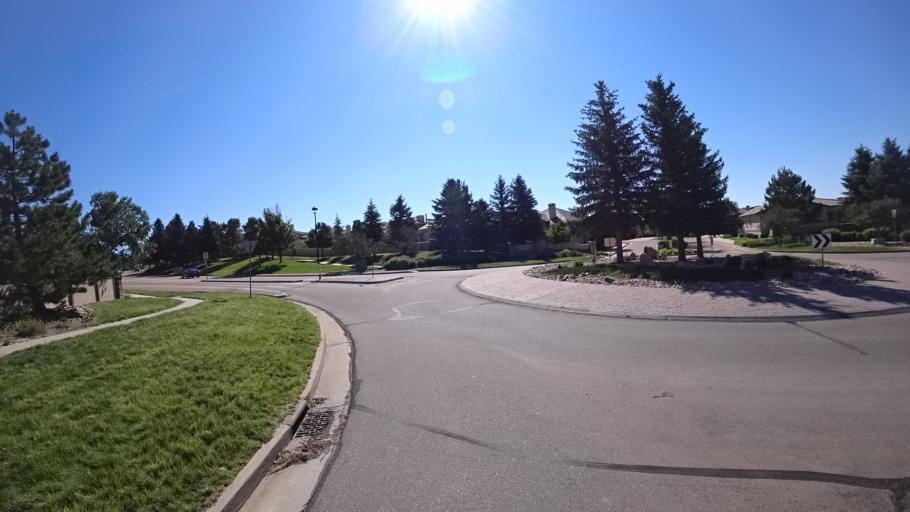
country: US
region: Colorado
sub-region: El Paso County
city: Gleneagle
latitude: 38.9737
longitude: -104.7832
